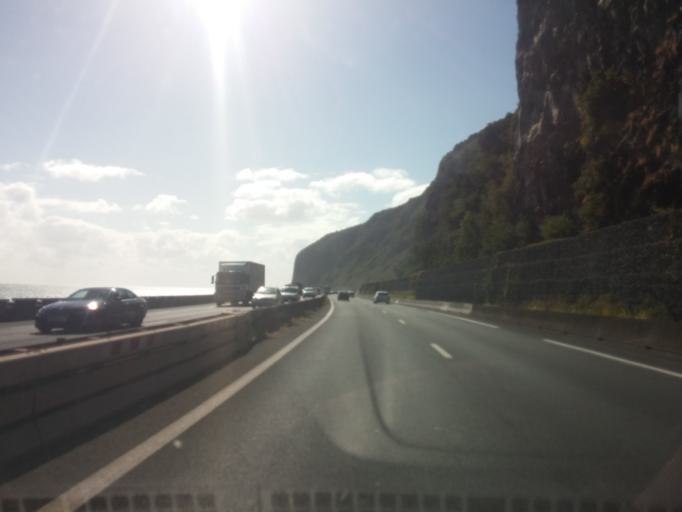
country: RE
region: Reunion
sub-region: Reunion
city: La Possession
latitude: -20.8907
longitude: 55.3848
